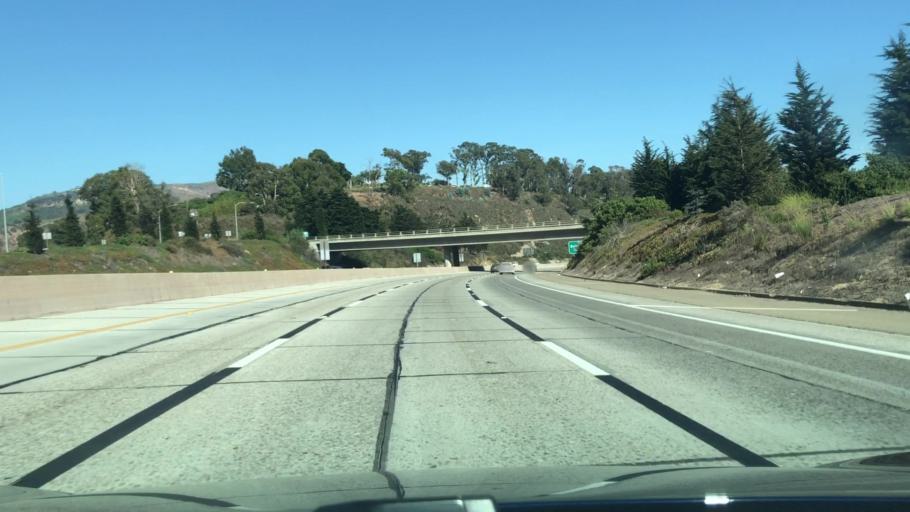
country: US
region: California
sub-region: Santa Barbara County
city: Carpinteria
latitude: 34.3844
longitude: -119.4862
